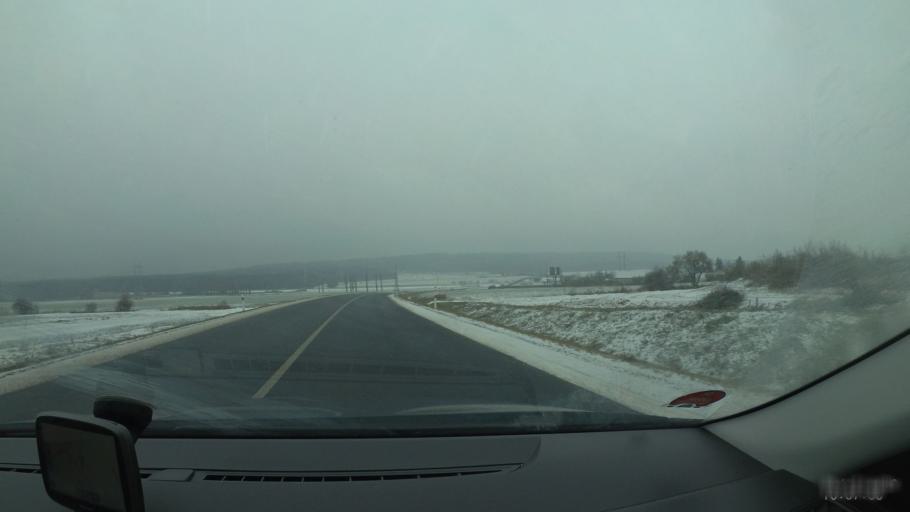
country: CZ
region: Central Bohemia
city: Revnicov
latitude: 50.1827
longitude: 13.8160
